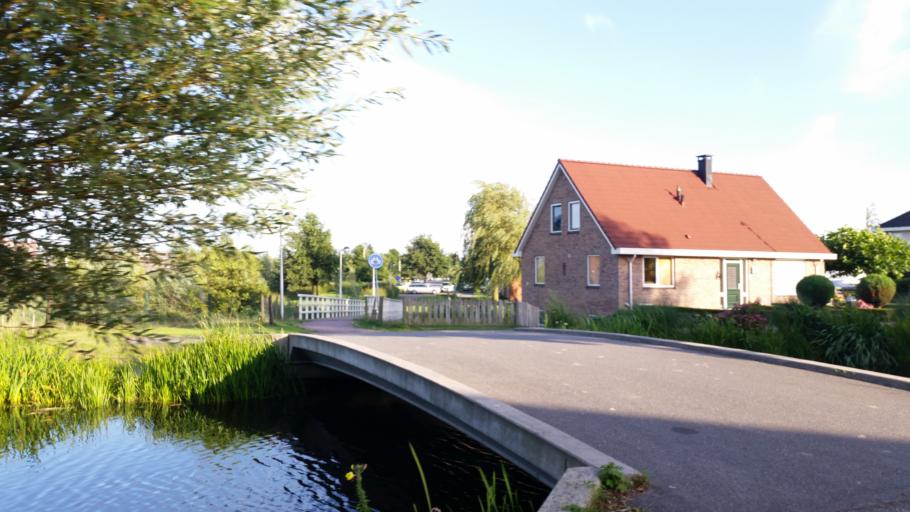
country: NL
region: South Holland
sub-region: Gemeente Den Haag
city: Ypenburg
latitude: 52.0506
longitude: 4.4069
